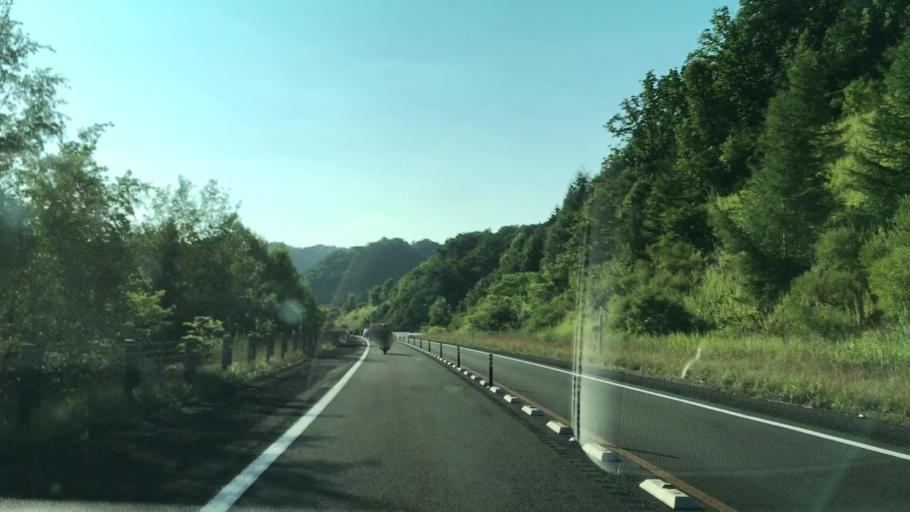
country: JP
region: Hokkaido
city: Chitose
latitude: 42.9129
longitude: 141.9756
